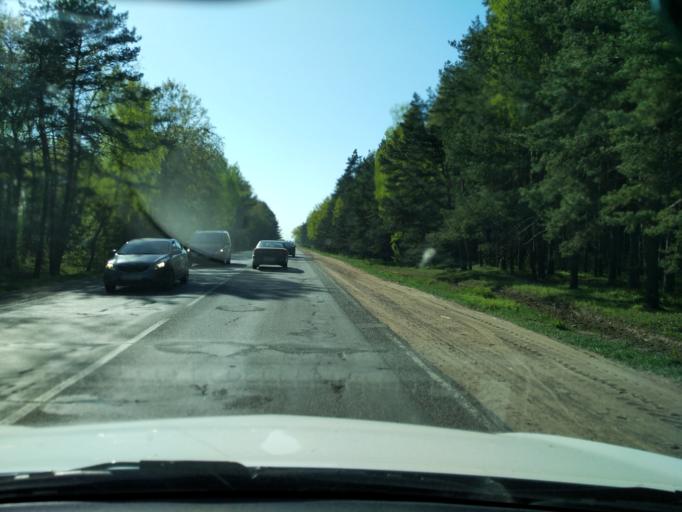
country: BY
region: Minsk
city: Borovlyany
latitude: 53.9657
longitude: 27.6586
